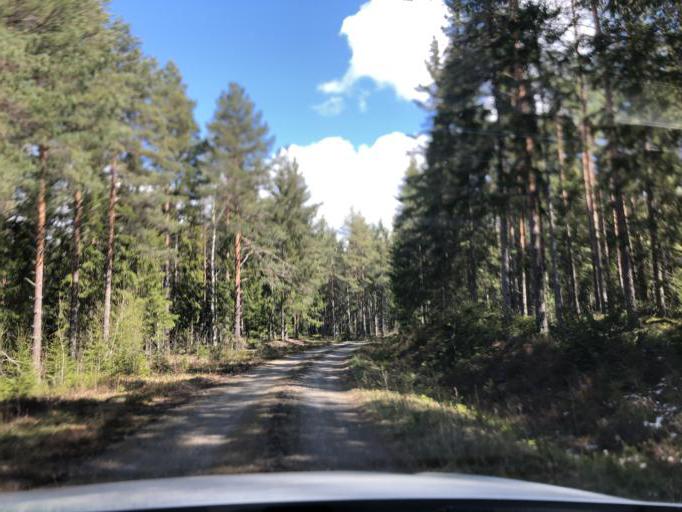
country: SE
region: Dalarna
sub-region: Avesta Kommun
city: Horndal
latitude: 60.2293
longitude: 16.5946
